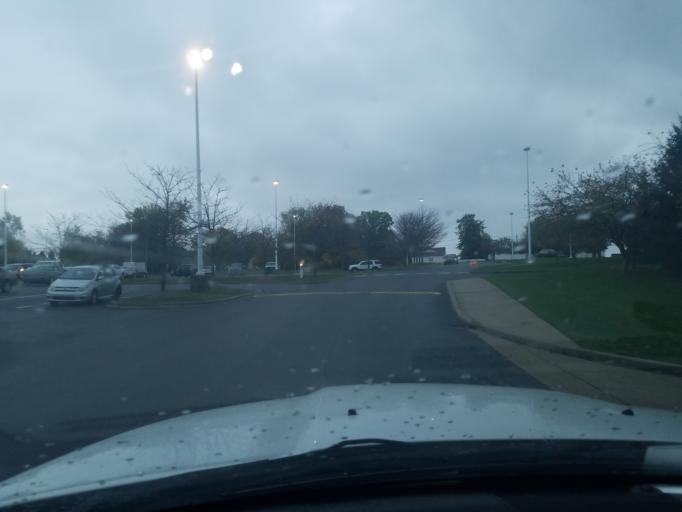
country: US
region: Indiana
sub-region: Floyd County
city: New Albany
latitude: 38.2993
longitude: -85.8102
